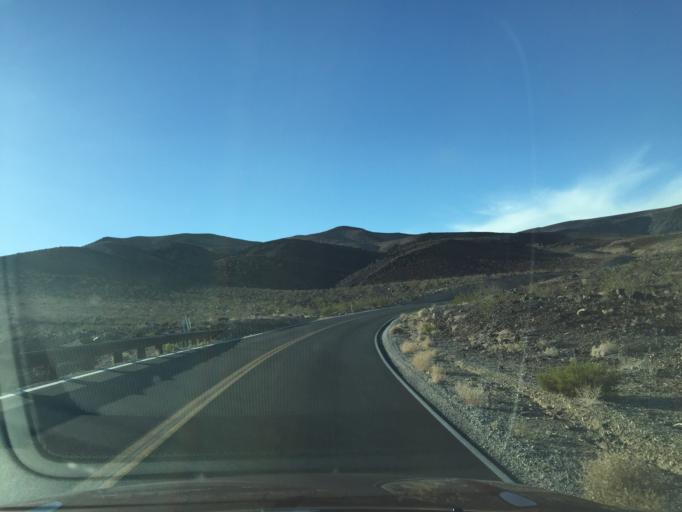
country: US
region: California
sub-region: San Bernardino County
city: Searles Valley
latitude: 36.3480
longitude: -117.5269
